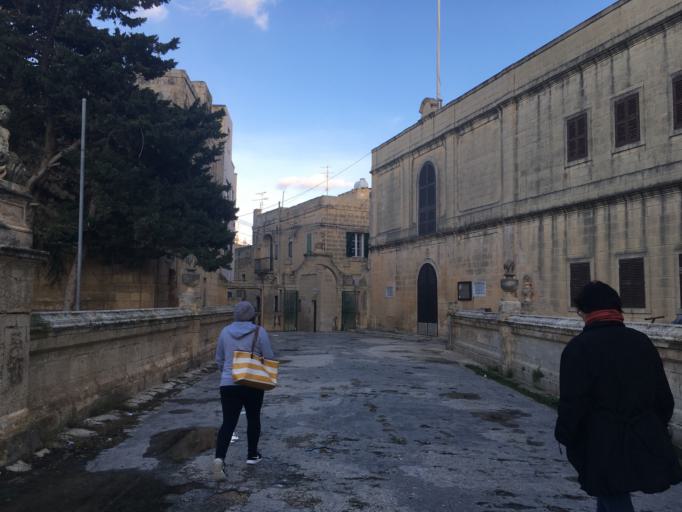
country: MT
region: Ir-Rabat
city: Rabat
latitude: 35.8821
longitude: 14.3997
